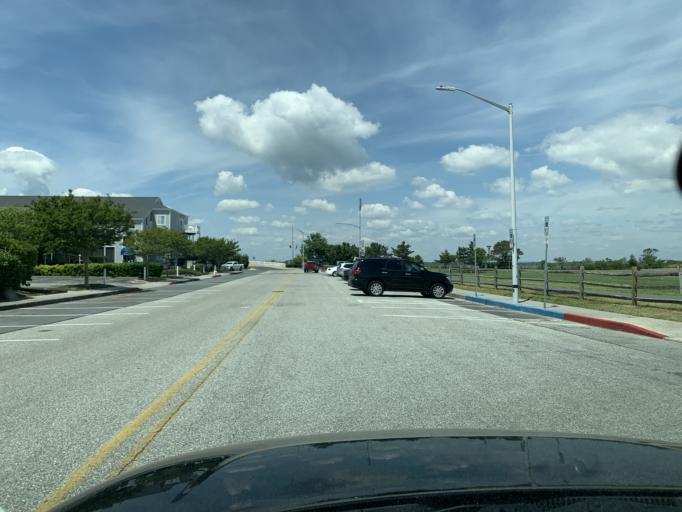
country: US
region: Maryland
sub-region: Worcester County
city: Ocean City
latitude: 38.4308
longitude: -75.0592
